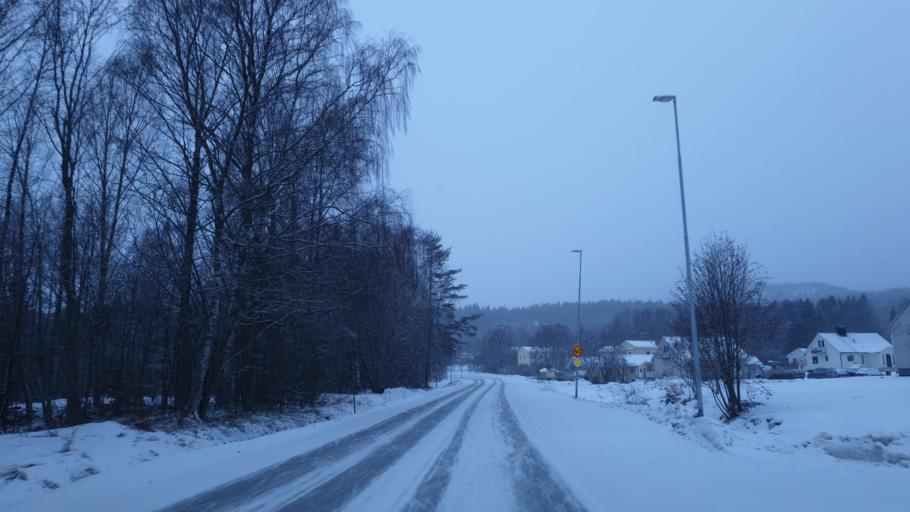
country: SE
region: Vaesternorrland
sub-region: OErnskoeldsviks Kommun
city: Ornskoldsvik
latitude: 63.3001
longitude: 18.6400
